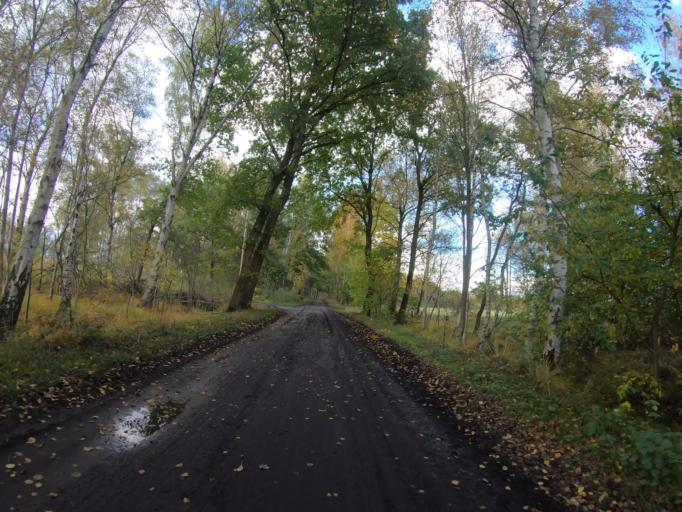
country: DE
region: Lower Saxony
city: Wagenhoff
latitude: 52.5510
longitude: 10.5567
